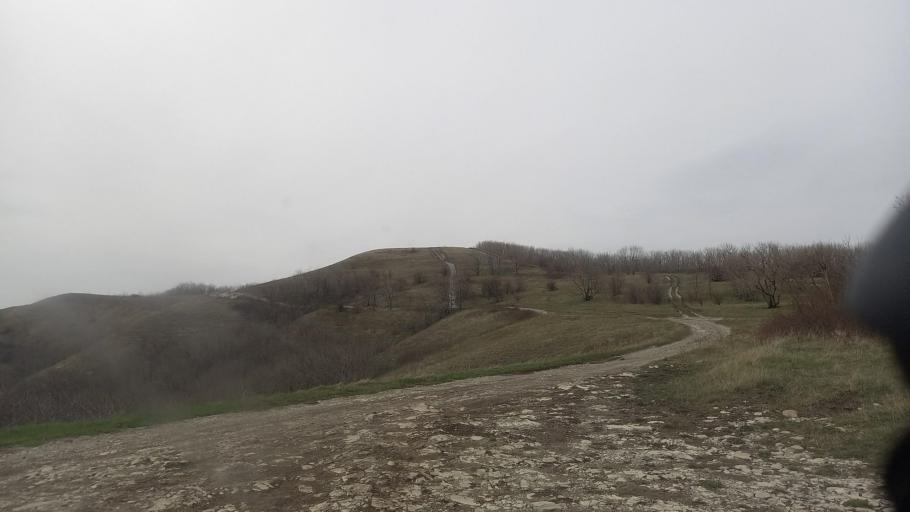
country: RU
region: Krasnodarskiy
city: Divnomorskoye
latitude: 44.6091
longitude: 38.2428
